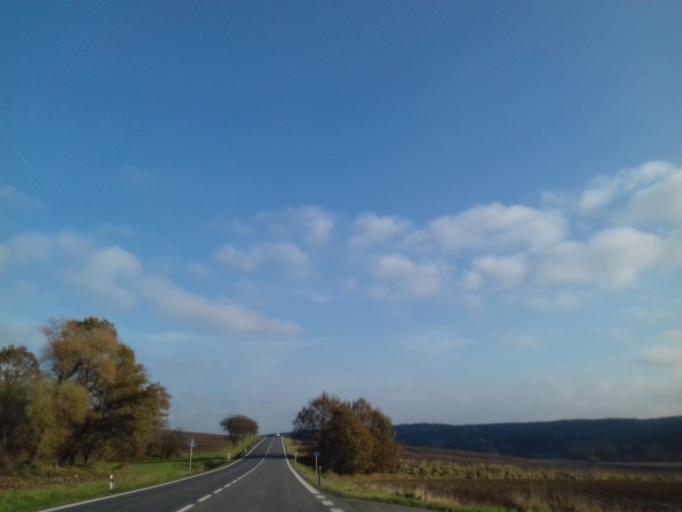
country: CZ
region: Plzensky
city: Blizejov
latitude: 49.5377
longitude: 12.9898
